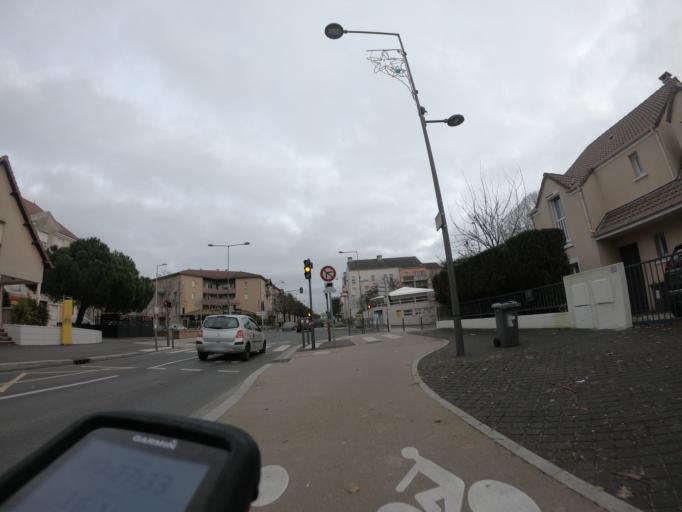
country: FR
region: Ile-de-France
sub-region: Departement du Val-de-Marne
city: Chevilly-Larue
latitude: 48.7705
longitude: 2.3631
